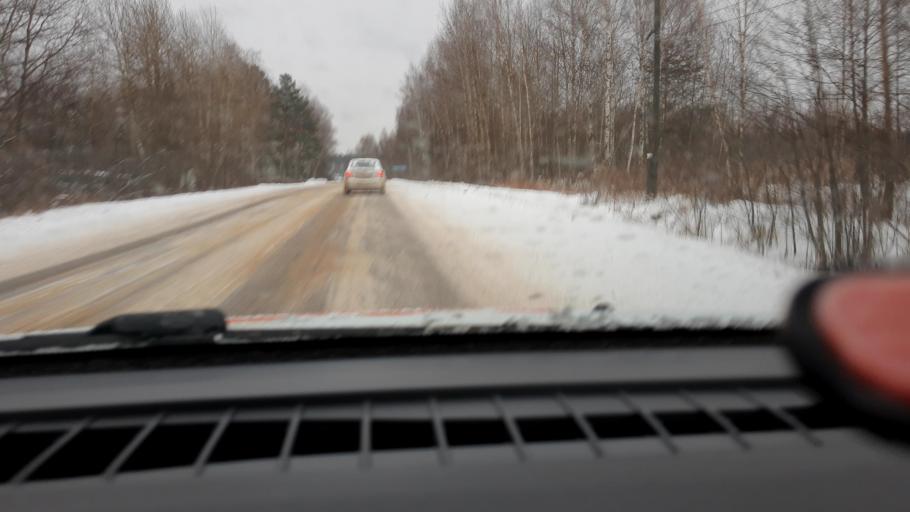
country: RU
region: Nizjnij Novgorod
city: Kstovo
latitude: 56.2778
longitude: 44.3553
